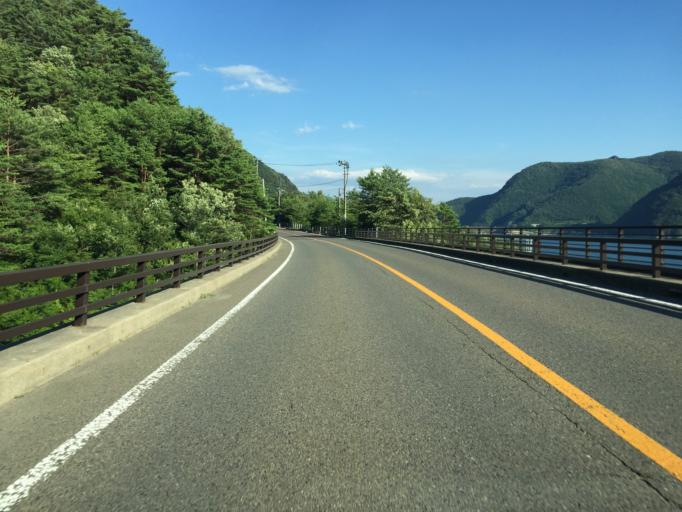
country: JP
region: Miyagi
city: Shiroishi
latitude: 37.9743
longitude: 140.4994
